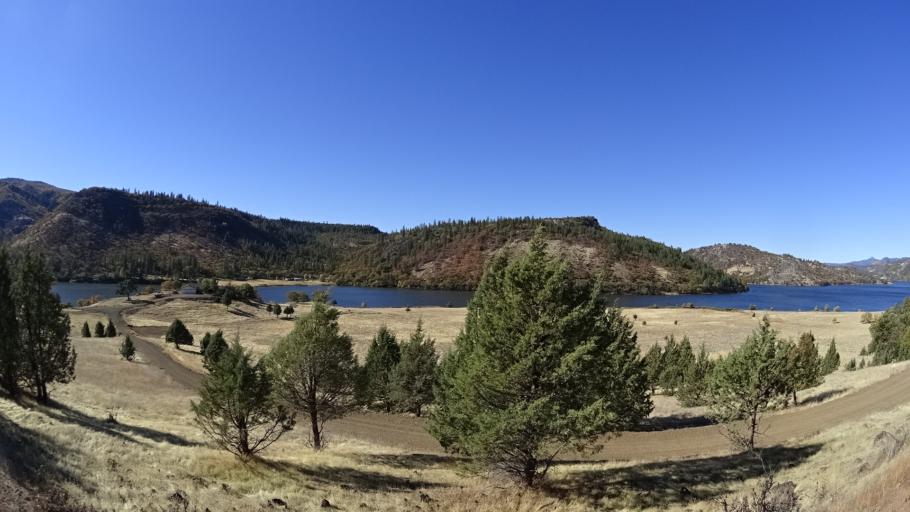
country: US
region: California
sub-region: Siskiyou County
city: Montague
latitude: 41.9753
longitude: -122.2804
